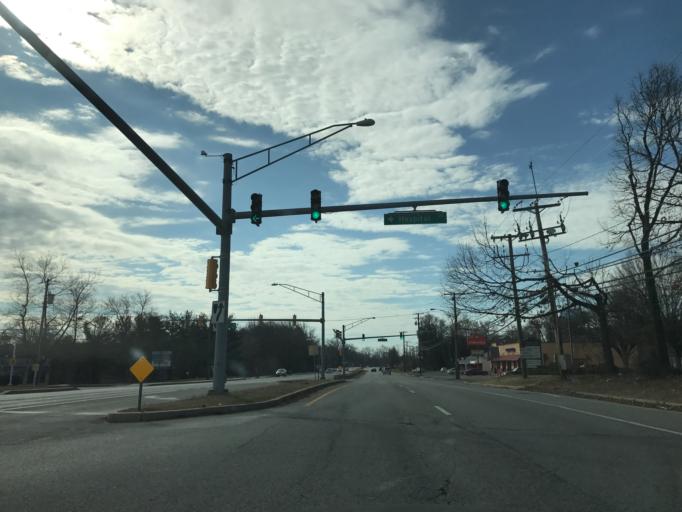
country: US
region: Maryland
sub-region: Anne Arundel County
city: South Gate
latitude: 39.1420
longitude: -76.6325
